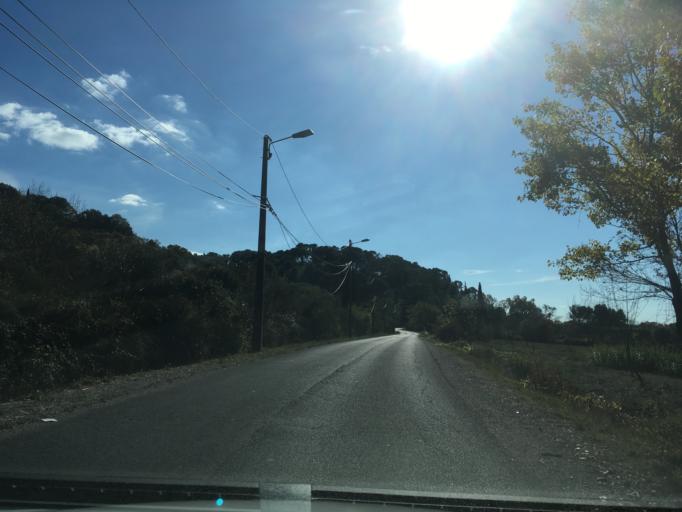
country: FR
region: Languedoc-Roussillon
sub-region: Departement de l'Herault
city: Juvignac
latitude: 43.6069
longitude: 3.8216
